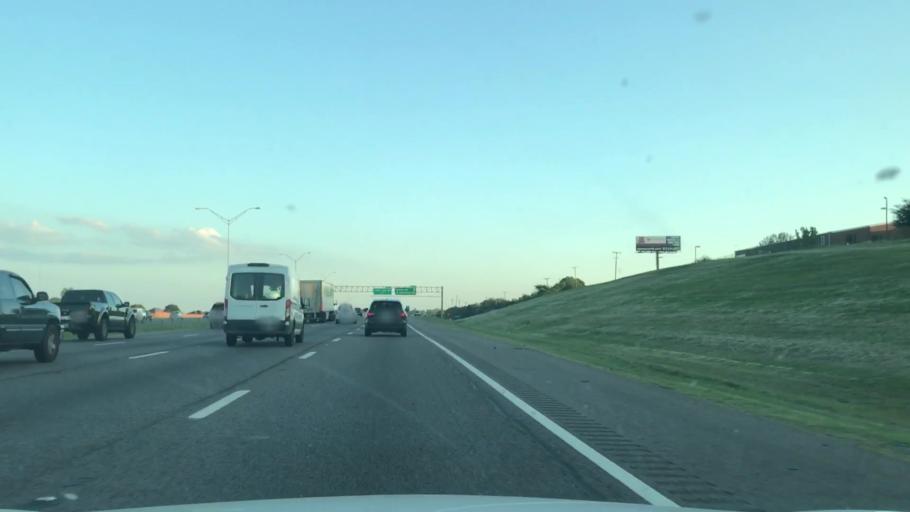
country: US
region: Texas
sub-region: Dallas County
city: Mesquite
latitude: 32.7546
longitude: -96.6169
